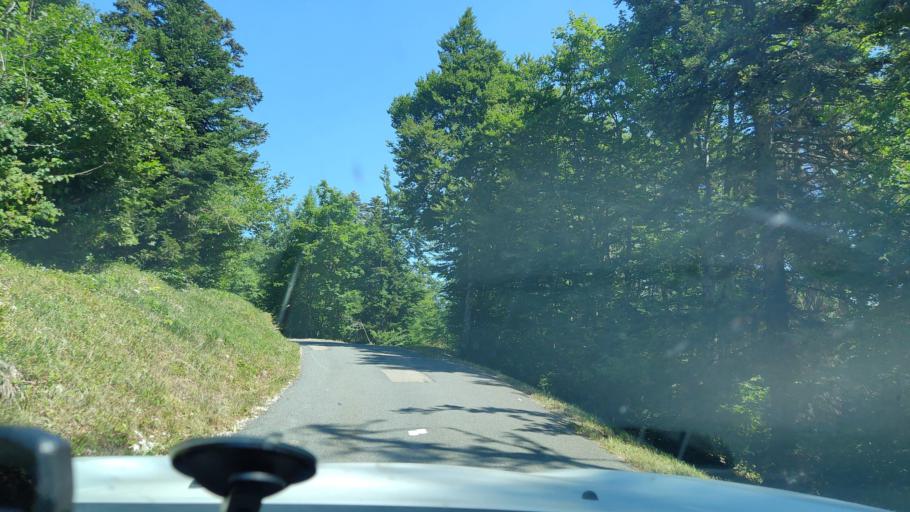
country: FR
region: Rhone-Alpes
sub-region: Departement de la Savoie
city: Le Bourget-du-Lac
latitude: 45.6564
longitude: 5.8246
